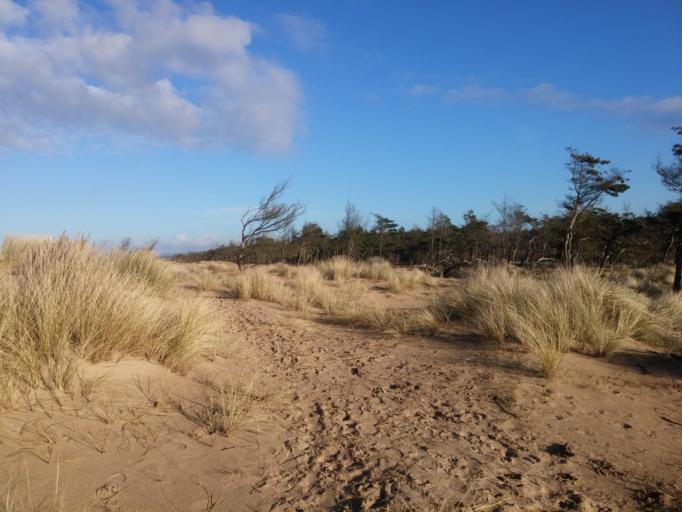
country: SE
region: Skane
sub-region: Angelholms Kommun
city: AEngelholm
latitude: 56.2379
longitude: 12.8165
